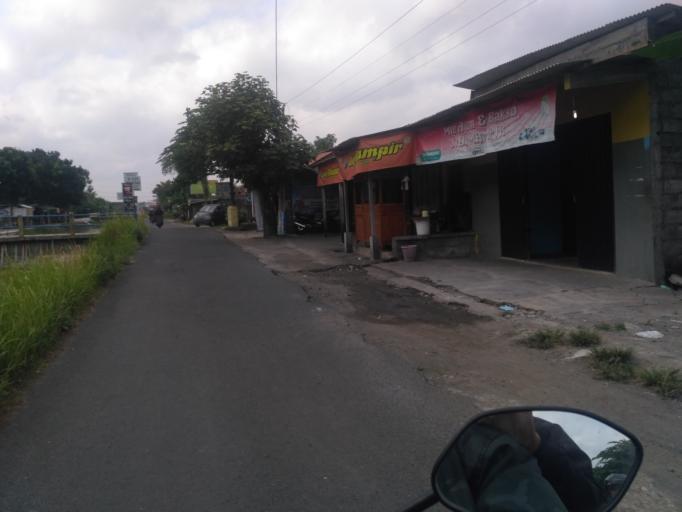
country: ID
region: Daerah Istimewa Yogyakarta
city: Yogyakarta
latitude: -7.7579
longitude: 110.3578
